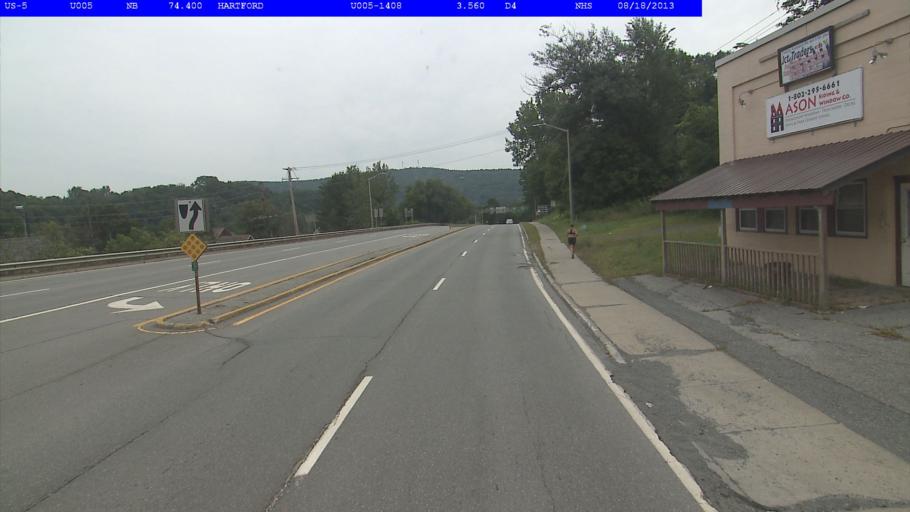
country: US
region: Vermont
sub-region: Windsor County
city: White River Junction
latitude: 43.6520
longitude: -72.3287
